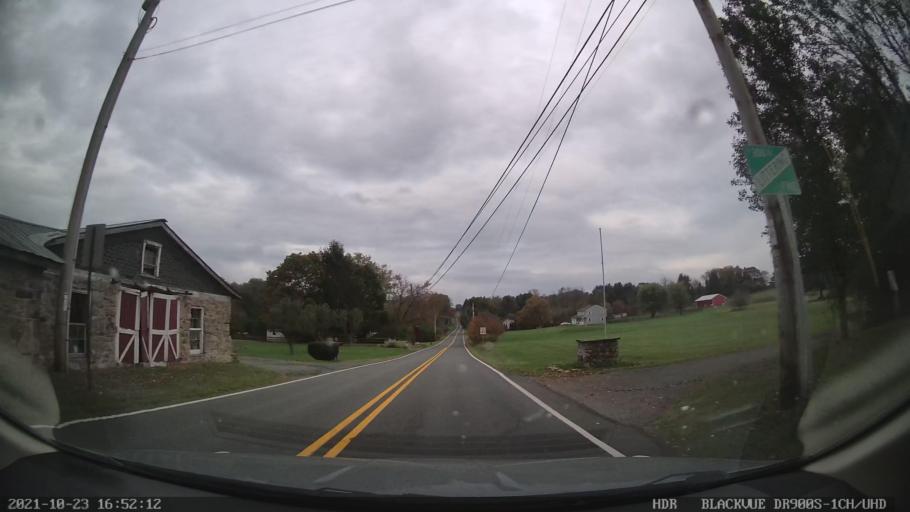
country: US
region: Pennsylvania
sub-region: Berks County
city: Red Lion
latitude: 40.4668
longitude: -75.6022
